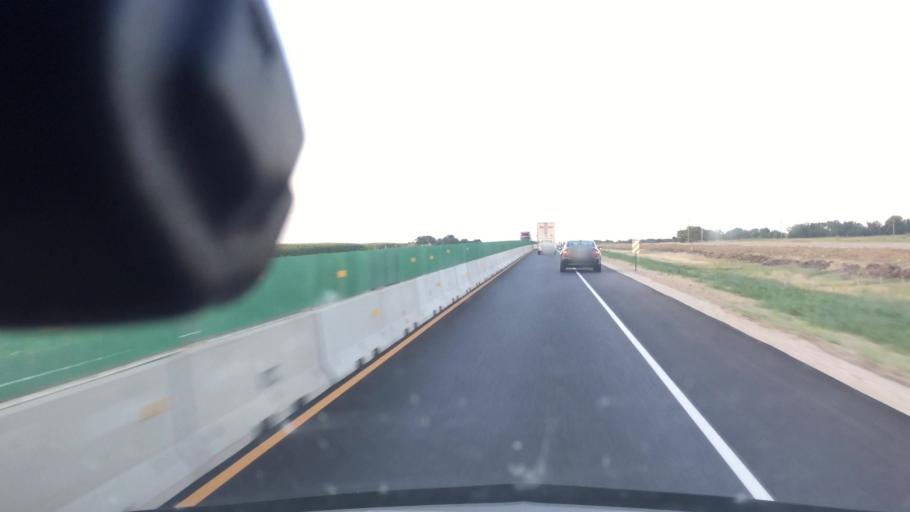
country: US
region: Illinois
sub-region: Livingston County
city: Pontiac
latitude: 40.9344
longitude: -88.6093
